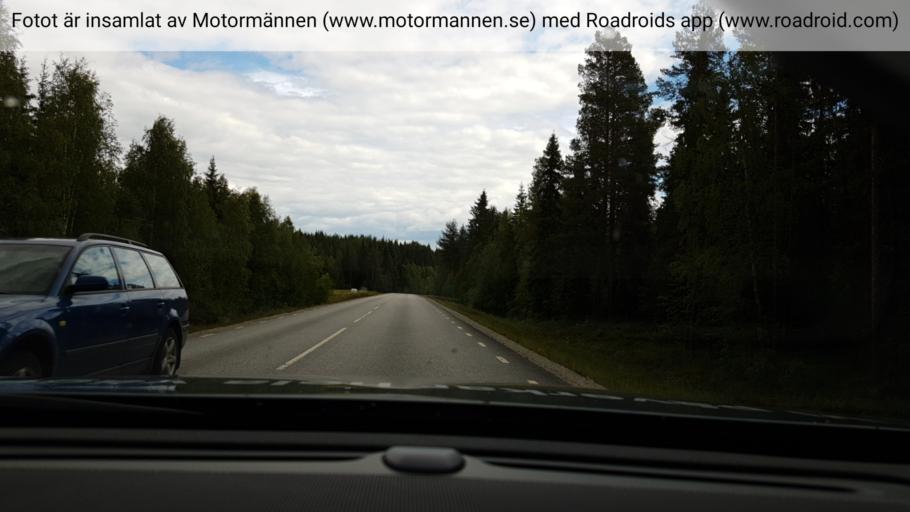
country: SE
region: Vaesterbotten
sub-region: Vindelns Kommun
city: Vindeln
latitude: 64.2086
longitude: 19.6639
